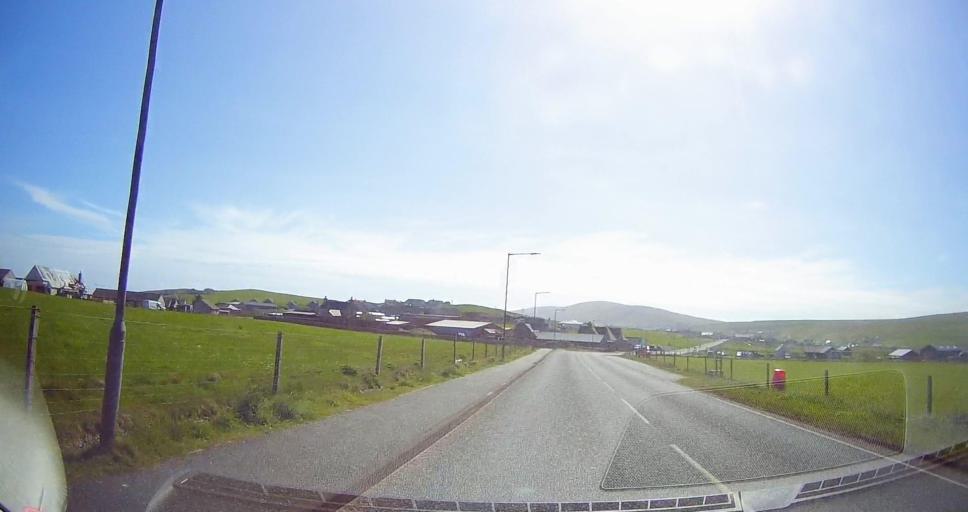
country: GB
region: Scotland
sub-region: Shetland Islands
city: Sandwick
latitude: 60.0041
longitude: -1.2325
